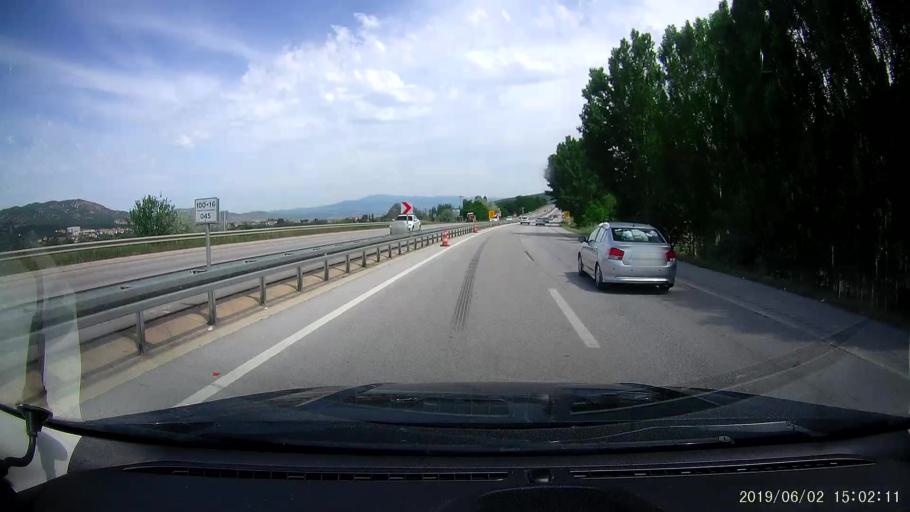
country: TR
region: Corum
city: Osmancik
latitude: 40.9837
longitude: 34.7628
